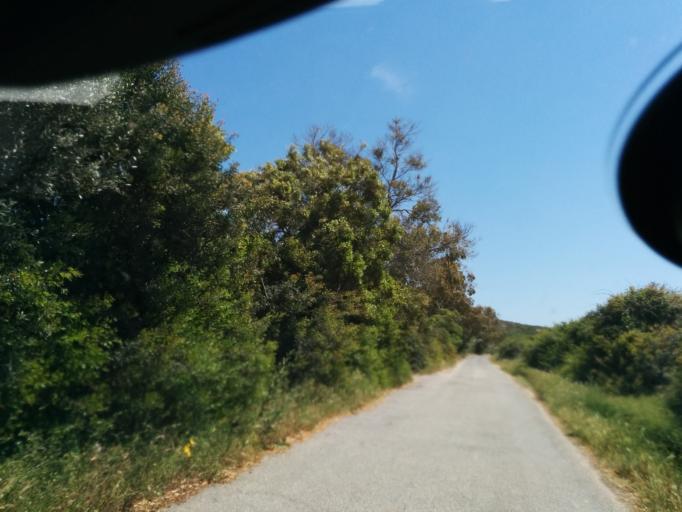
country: IT
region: Sardinia
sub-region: Provincia di Carbonia-Iglesias
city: Calasetta
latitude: 39.0613
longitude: 8.3798
